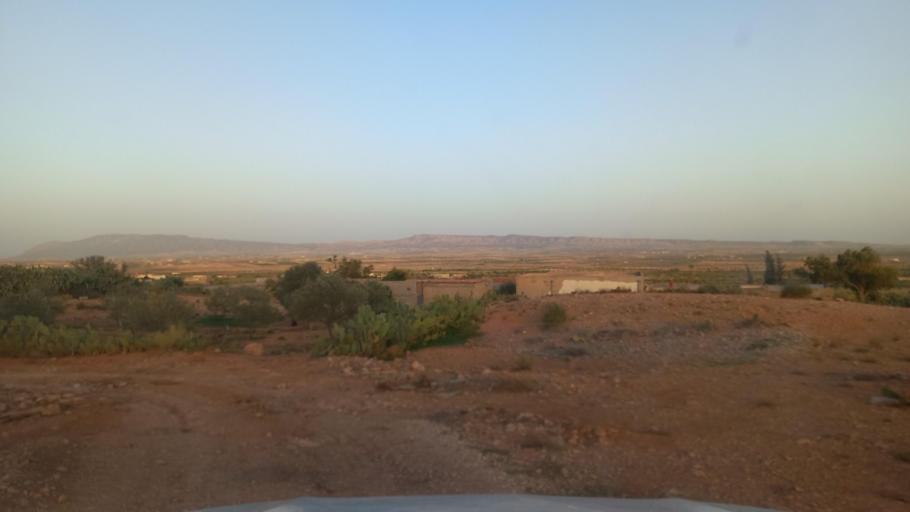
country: TN
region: Al Qasrayn
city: Sbiba
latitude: 35.3753
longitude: 9.0072
